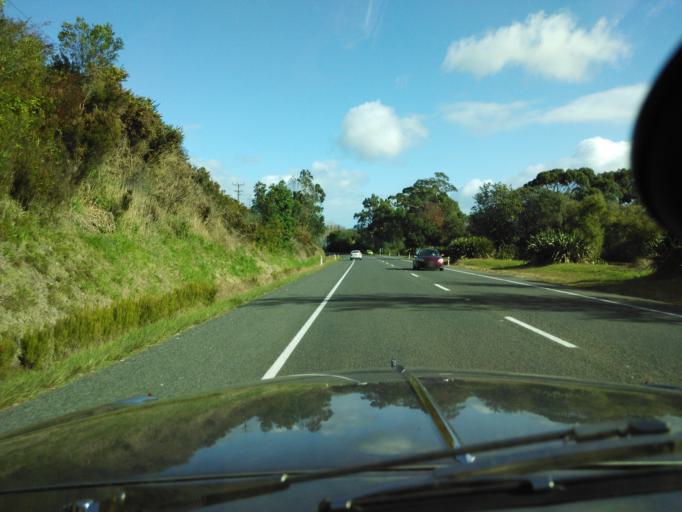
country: NZ
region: Waikato
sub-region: Hauraki District
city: Paeroa
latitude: -37.5913
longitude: 175.6475
